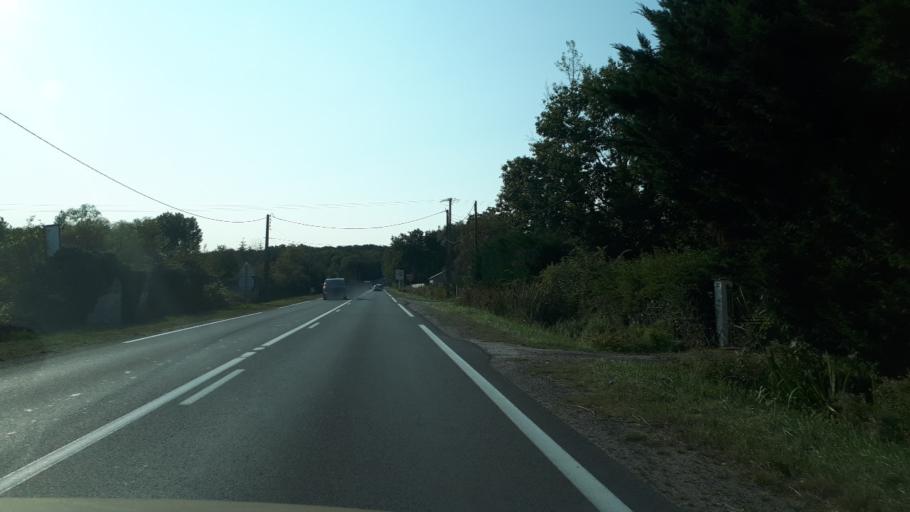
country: FR
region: Centre
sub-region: Departement du Cher
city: Vignoux-sur-Barangeon
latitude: 47.2040
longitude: 2.1679
